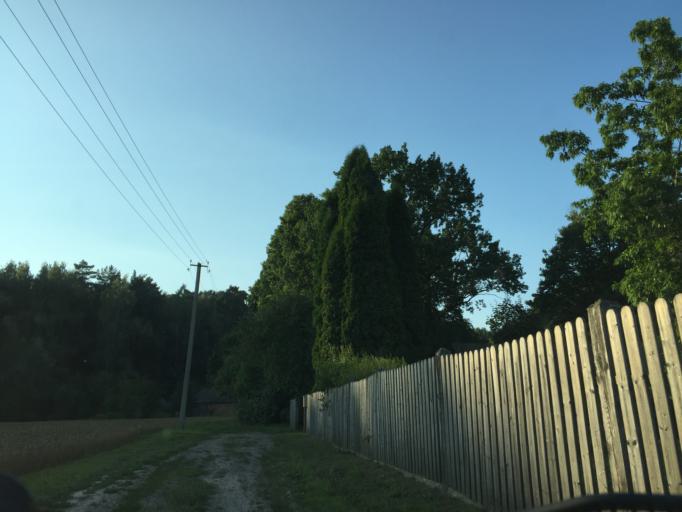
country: LV
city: Tervete
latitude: 56.4727
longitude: 23.3754
